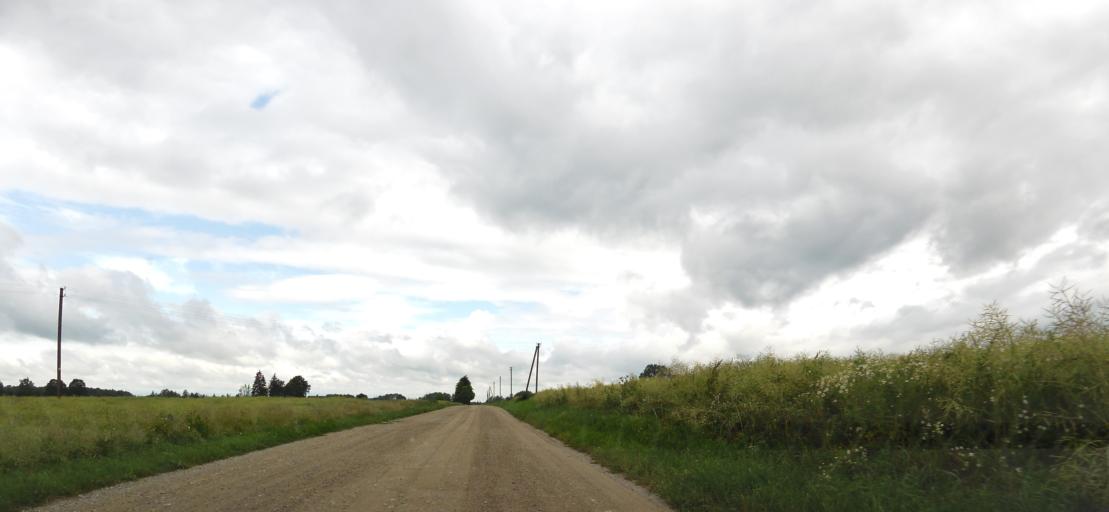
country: LT
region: Panevezys
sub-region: Birzai
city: Birzai
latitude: 56.1794
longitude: 24.7054
